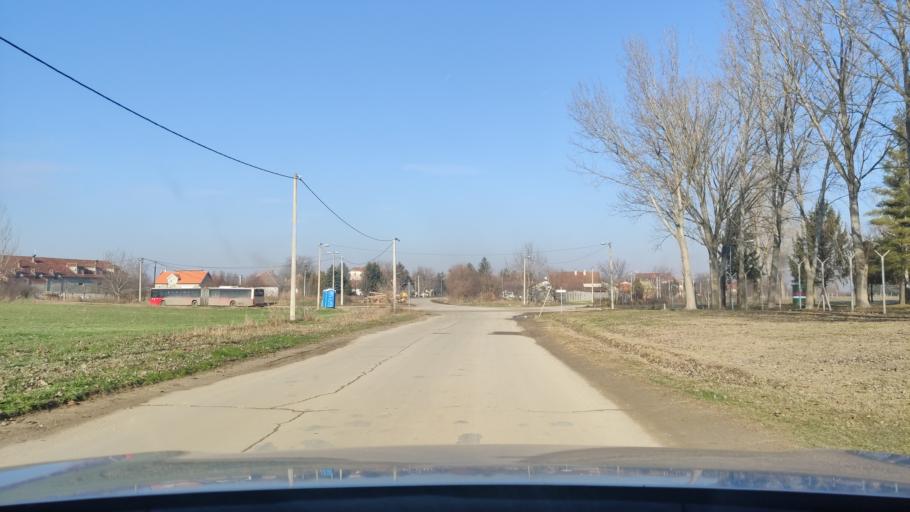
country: RS
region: Central Serbia
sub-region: Belgrade
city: Surcin
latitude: 44.7447
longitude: 20.2716
